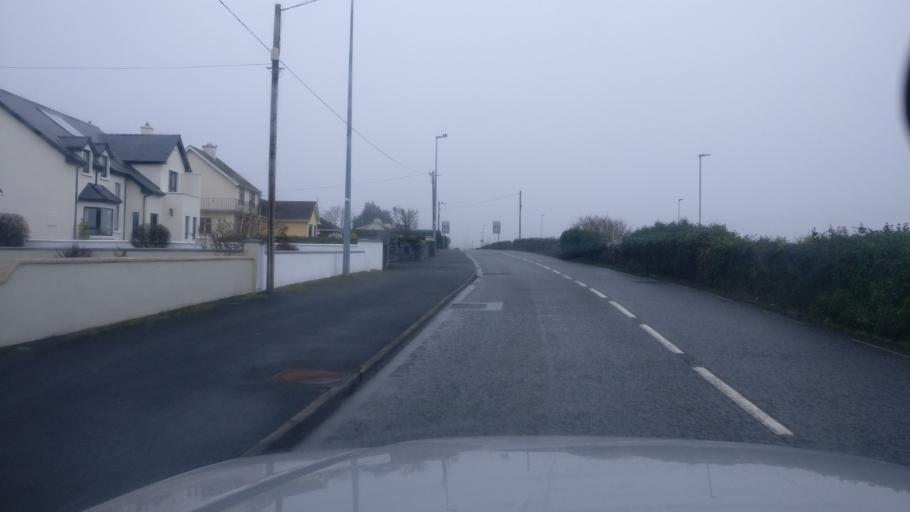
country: IE
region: Connaught
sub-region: County Galway
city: Loughrea
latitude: 53.1956
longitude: -8.5892
